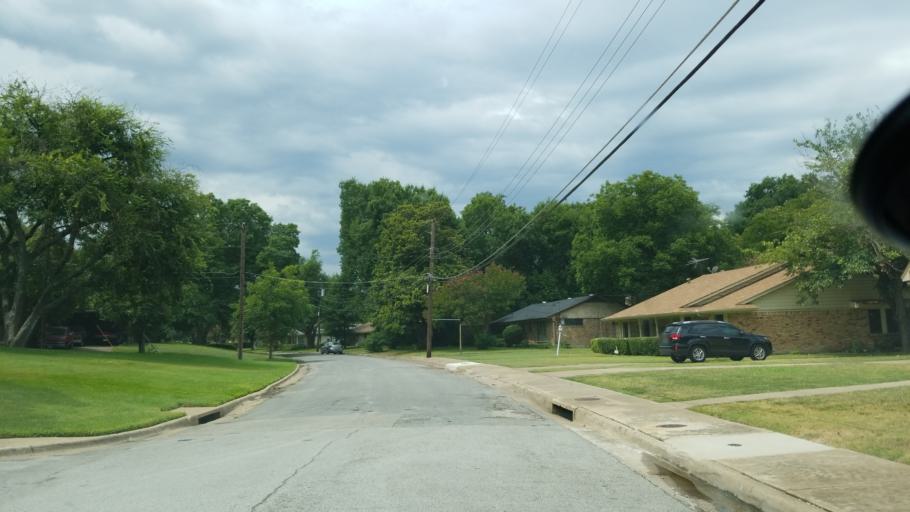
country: US
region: Texas
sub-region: Dallas County
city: Duncanville
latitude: 32.6682
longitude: -96.8415
